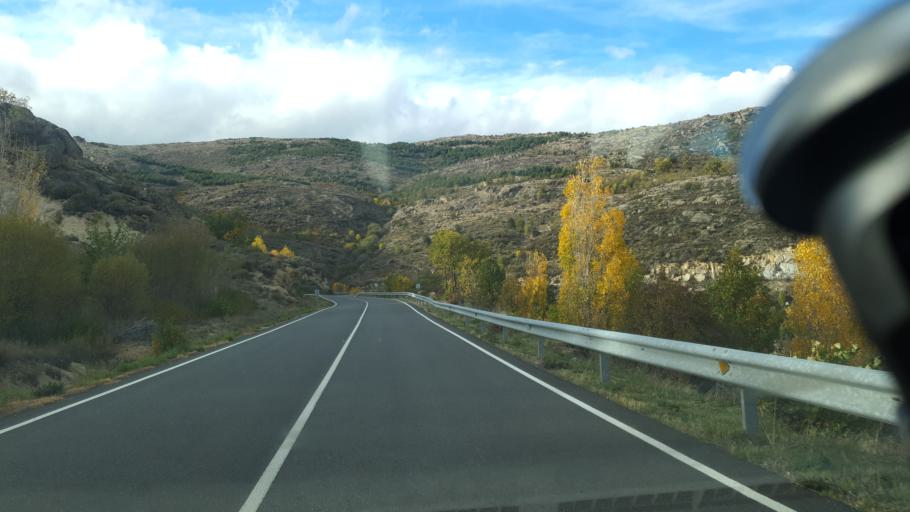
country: ES
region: Castille and Leon
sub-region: Provincia de Avila
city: Navaquesera
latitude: 40.4055
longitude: -4.9016
